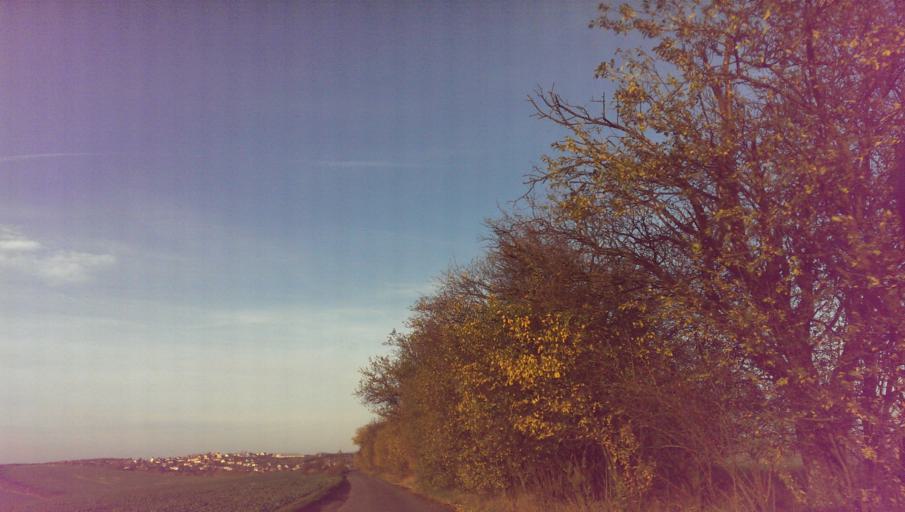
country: CZ
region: Zlin
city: Brezolupy
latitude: 49.1528
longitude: 17.5991
